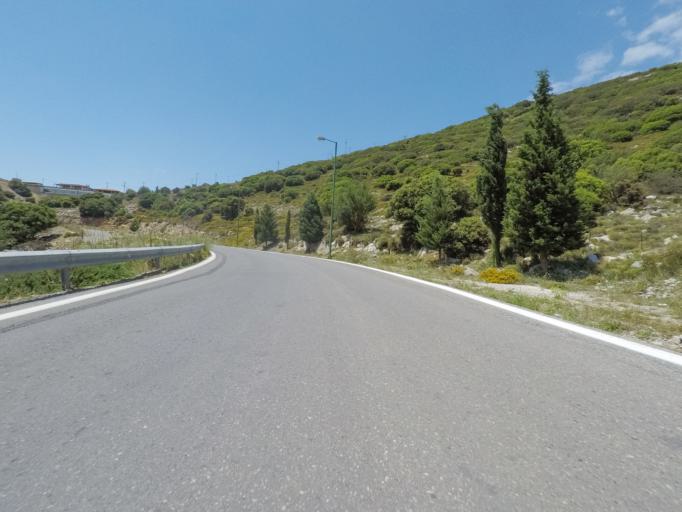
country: GR
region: Crete
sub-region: Nomos Irakleiou
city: Mokhos
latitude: 35.2030
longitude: 25.4584
